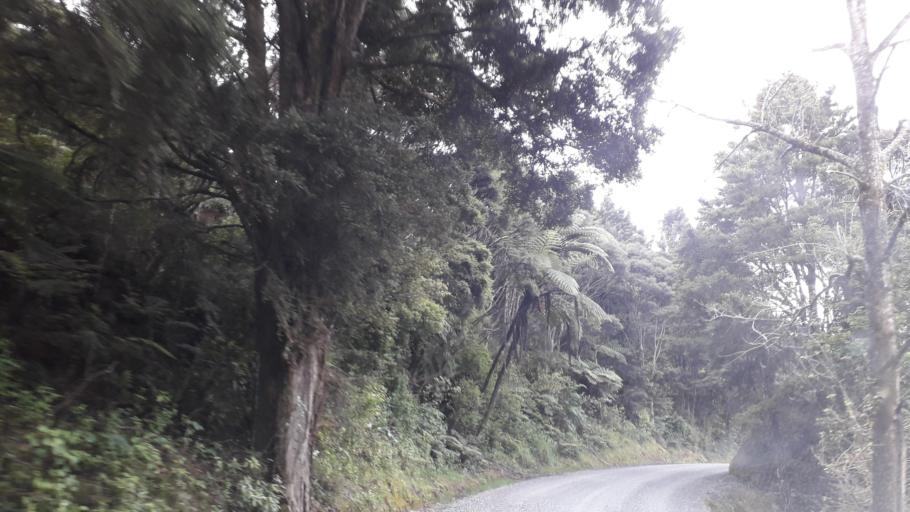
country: NZ
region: Northland
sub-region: Far North District
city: Taipa
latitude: -35.0599
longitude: 173.5506
